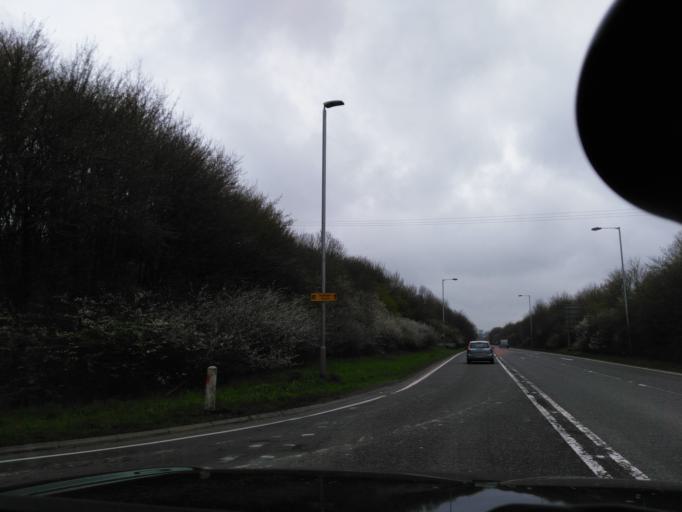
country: GB
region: England
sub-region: Somerset
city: Frome
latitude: 51.2246
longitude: -2.3016
